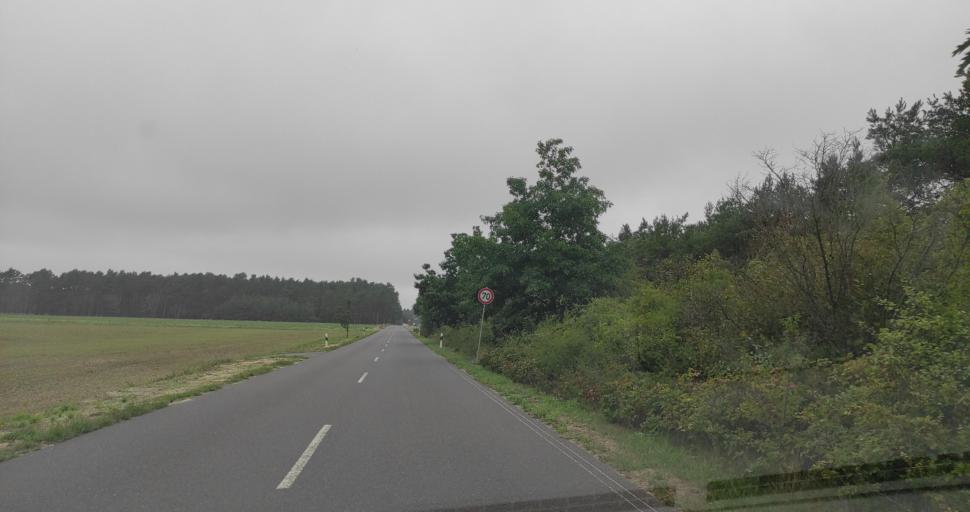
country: DE
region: Brandenburg
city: Forst
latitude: 51.7004
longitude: 14.5587
